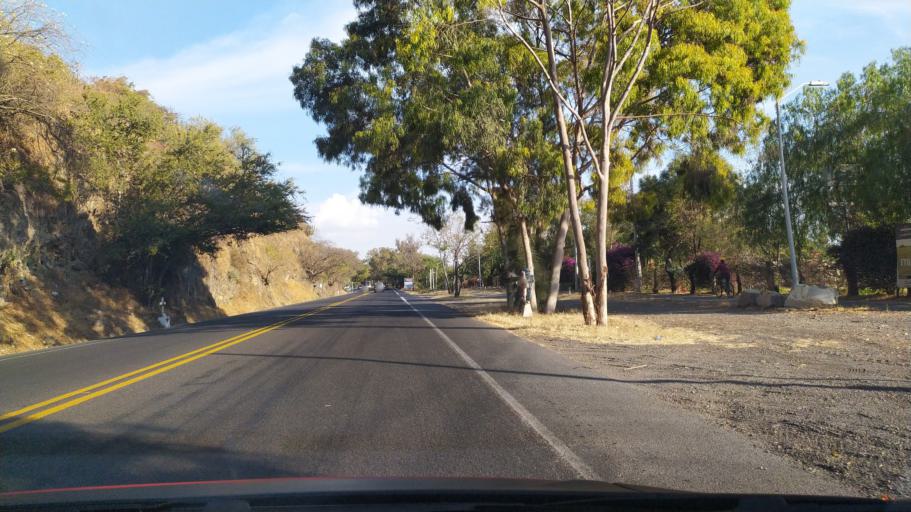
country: MX
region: Jalisco
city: Jamay
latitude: 20.2927
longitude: -102.7253
